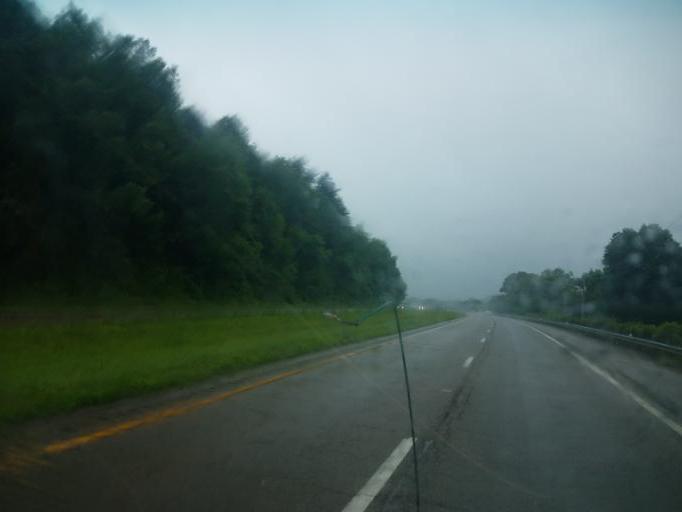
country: US
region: Ohio
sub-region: Tuscarawas County
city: Tuscarawas
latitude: 40.3921
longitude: -81.3817
